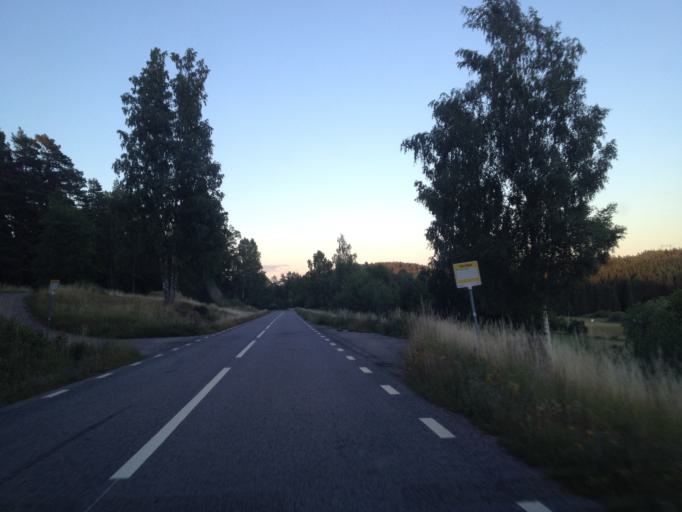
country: SE
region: Kalmar
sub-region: Vasterviks Kommun
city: Overum
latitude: 58.0239
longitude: 16.1202
